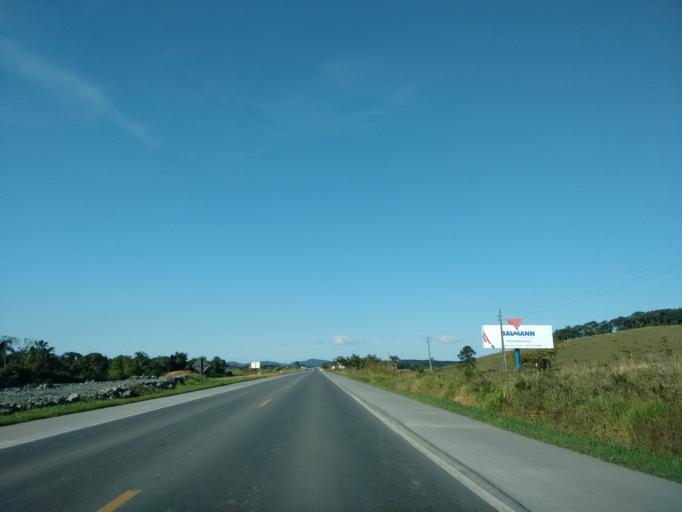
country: BR
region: Santa Catarina
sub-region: Guaramirim
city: Guaramirim
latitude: -26.4521
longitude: -48.8939
